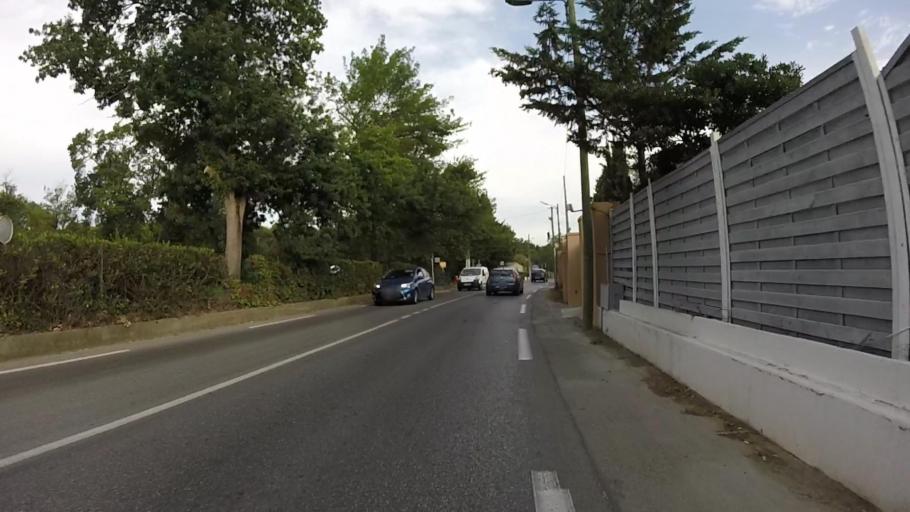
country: FR
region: Provence-Alpes-Cote d'Azur
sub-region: Departement des Alpes-Maritimes
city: Biot
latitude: 43.6174
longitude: 7.1039
